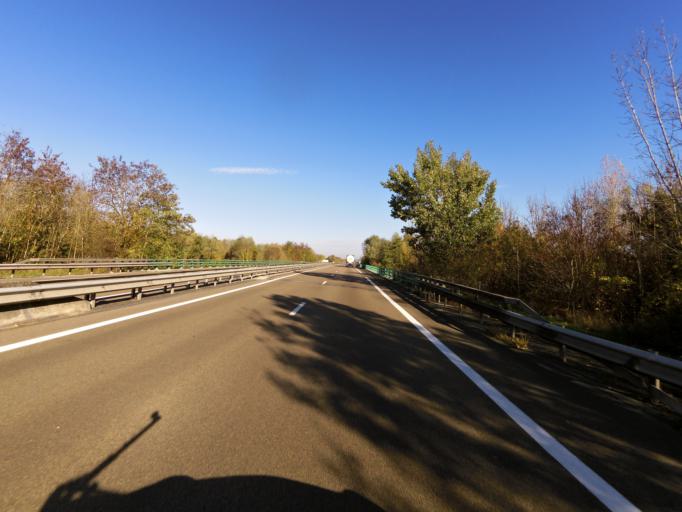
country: FR
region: Champagne-Ardenne
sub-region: Departement de la Marne
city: Fagnieres
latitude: 48.9925
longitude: 4.2957
